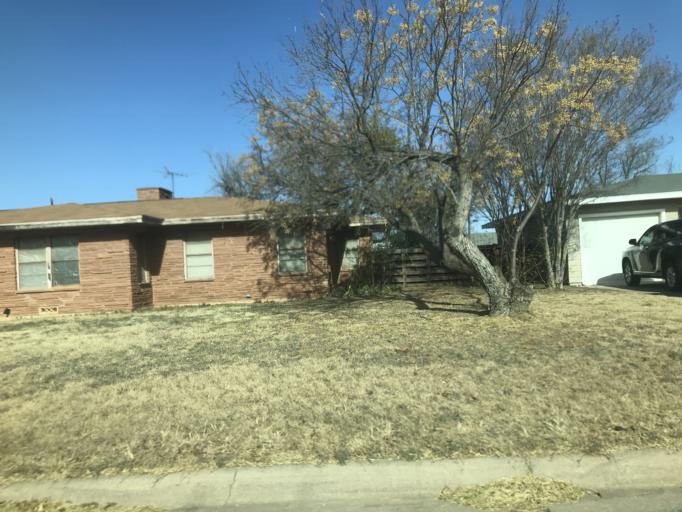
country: US
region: Texas
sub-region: Taylor County
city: Abilene
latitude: 32.4736
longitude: -99.7164
